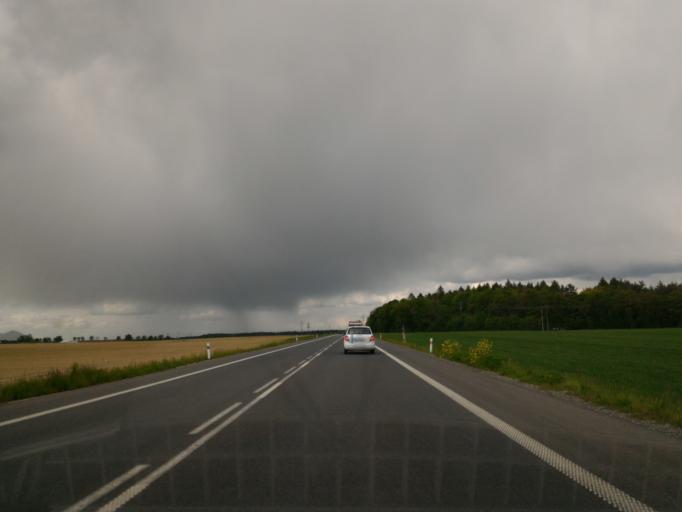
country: CZ
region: Central Bohemia
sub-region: Okres Mlada Boleslav
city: Mlada Boleslav
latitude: 50.4673
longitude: 14.8642
